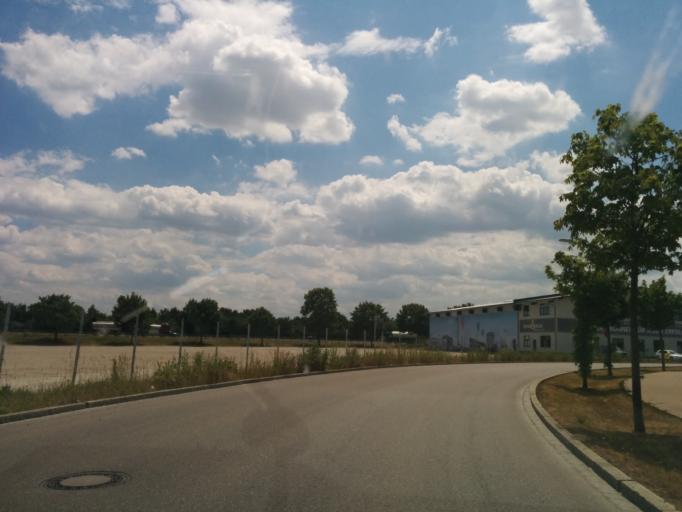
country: DE
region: Bavaria
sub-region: Swabia
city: Gersthofen
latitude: 48.4382
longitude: 10.8691
